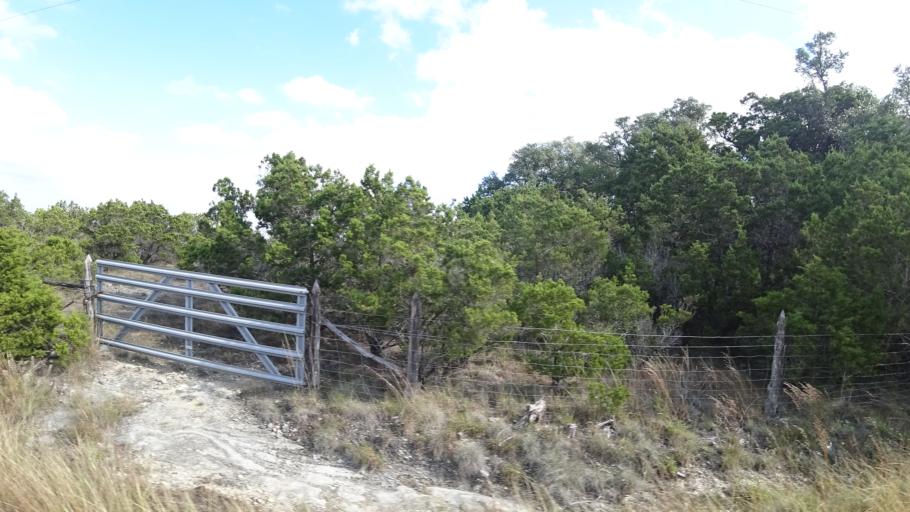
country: US
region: Texas
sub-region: Travis County
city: Bee Cave
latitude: 30.2562
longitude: -97.9347
